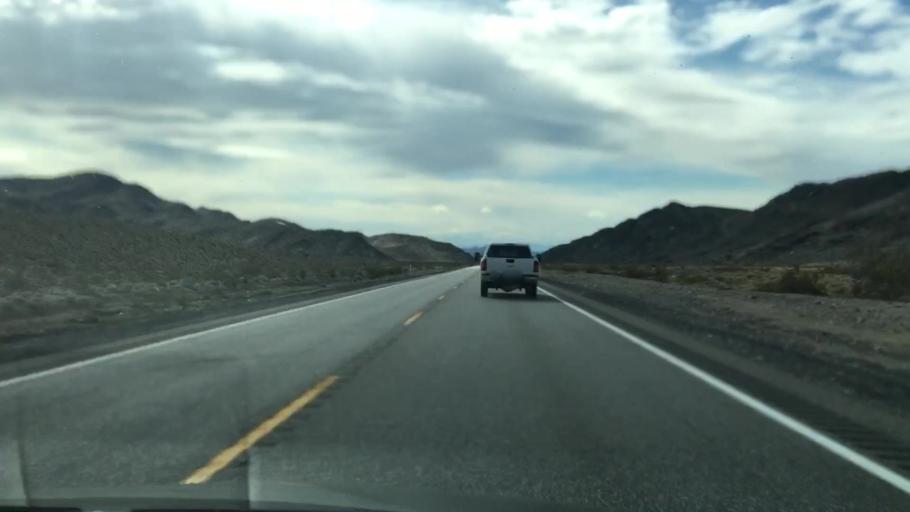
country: US
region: Nevada
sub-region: Nye County
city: Pahrump
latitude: 36.5795
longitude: -116.0676
